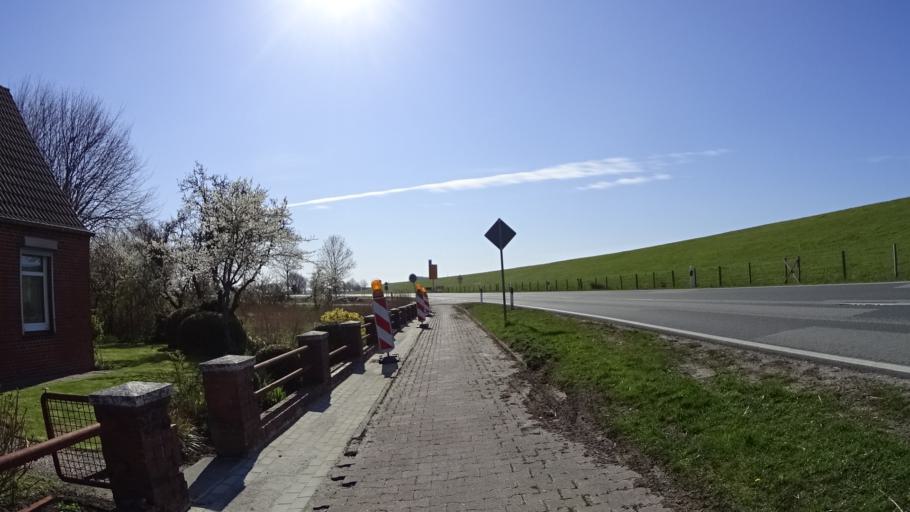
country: DE
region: Lower Saxony
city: Jemgum
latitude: 53.2967
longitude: 7.3927
